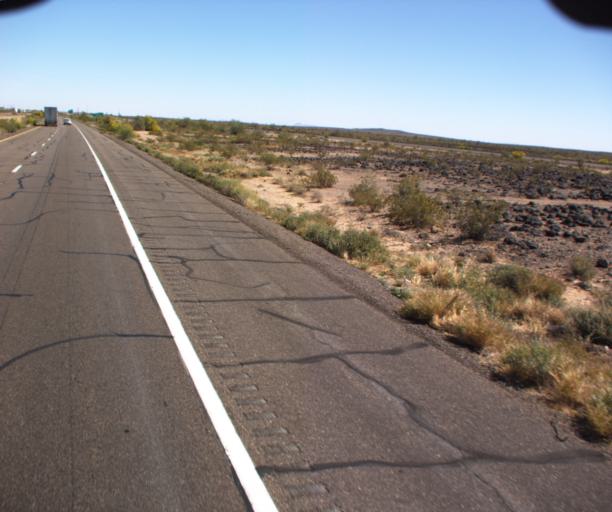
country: US
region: Arizona
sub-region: Maricopa County
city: Gila Bend
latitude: 32.8563
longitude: -113.2334
